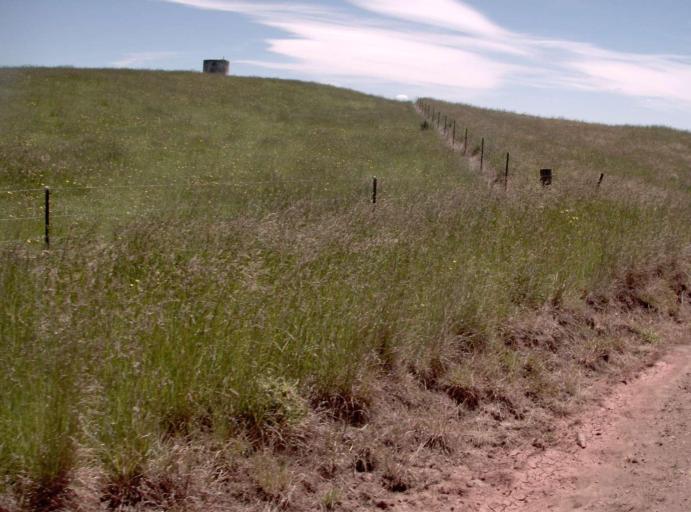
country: AU
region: New South Wales
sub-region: Snowy River
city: Jindabyne
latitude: -37.0928
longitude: 148.2535
